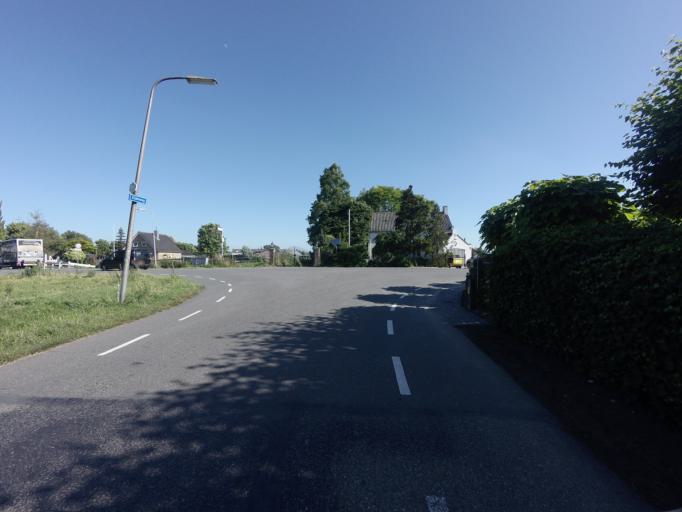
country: NL
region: South Holland
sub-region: Bodegraven-Reeuwijk
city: Reeuwijk
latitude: 52.0668
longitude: 4.7052
